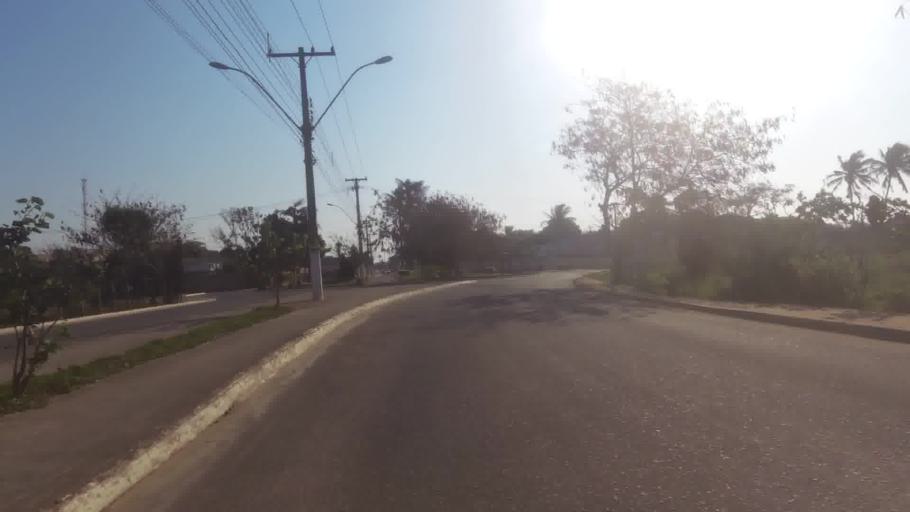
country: BR
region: Espirito Santo
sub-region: Itapemirim
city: Itapemirim
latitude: -21.0093
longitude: -40.8266
